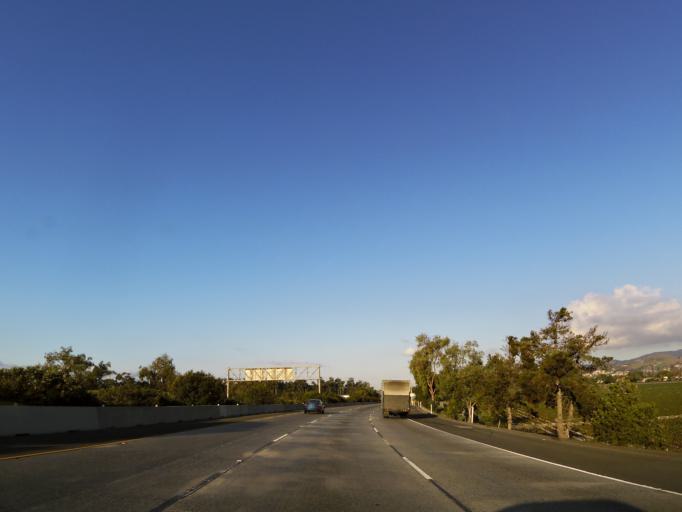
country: US
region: California
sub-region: Ventura County
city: Ventura
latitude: 34.2592
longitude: -119.2548
